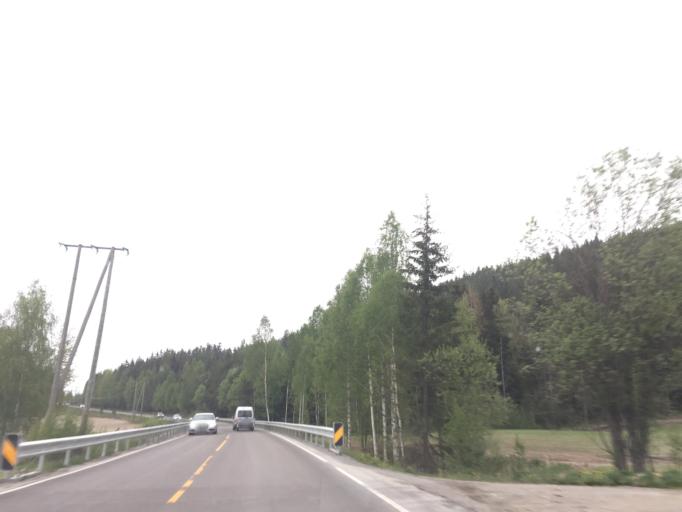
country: NO
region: Hedmark
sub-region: Sor-Odal
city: Skarnes
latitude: 60.2264
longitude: 11.6816
